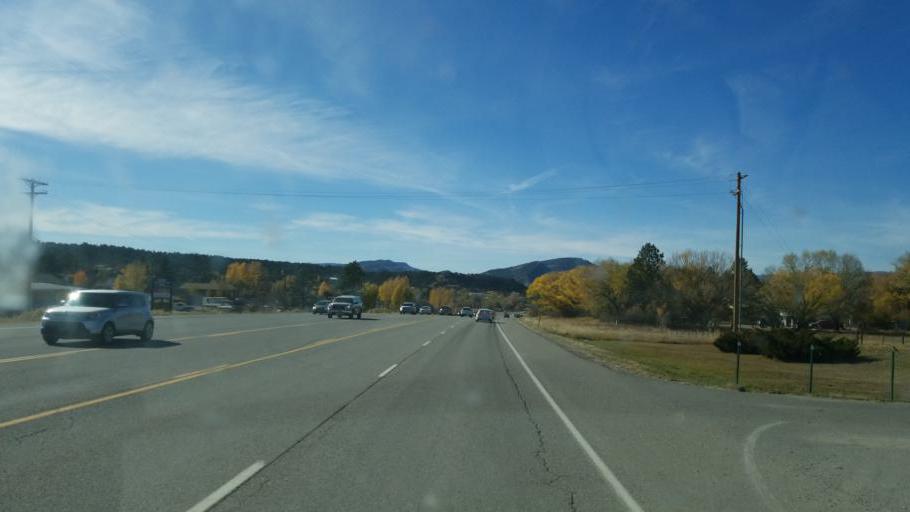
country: US
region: Colorado
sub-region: La Plata County
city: Durango
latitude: 37.2272
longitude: -107.8133
